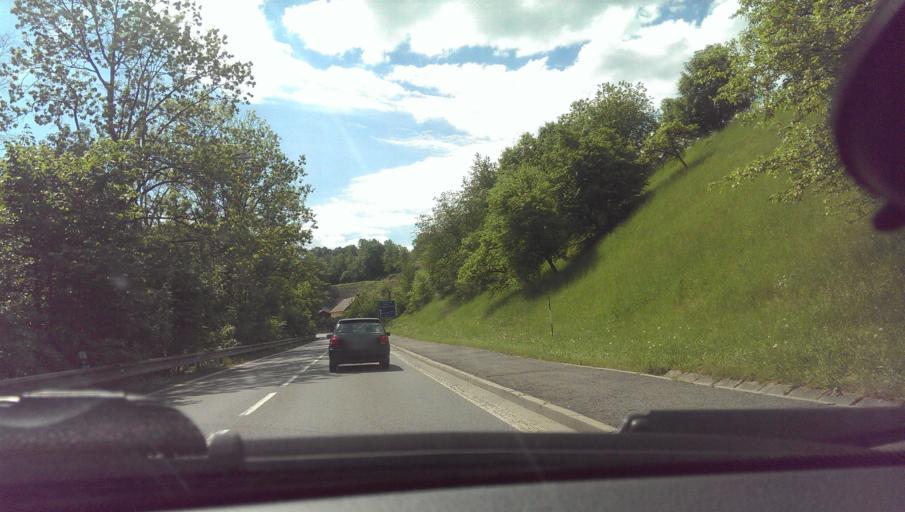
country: CZ
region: Zlin
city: Valasska Polanka
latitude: 49.2549
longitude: 17.9971
